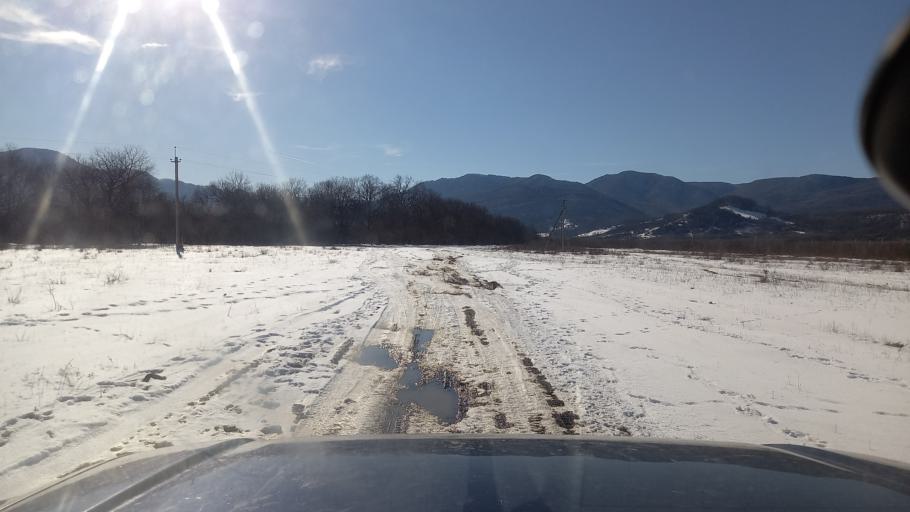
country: RU
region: Adygeya
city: Kamennomostskiy
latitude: 44.2191
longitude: 40.1799
